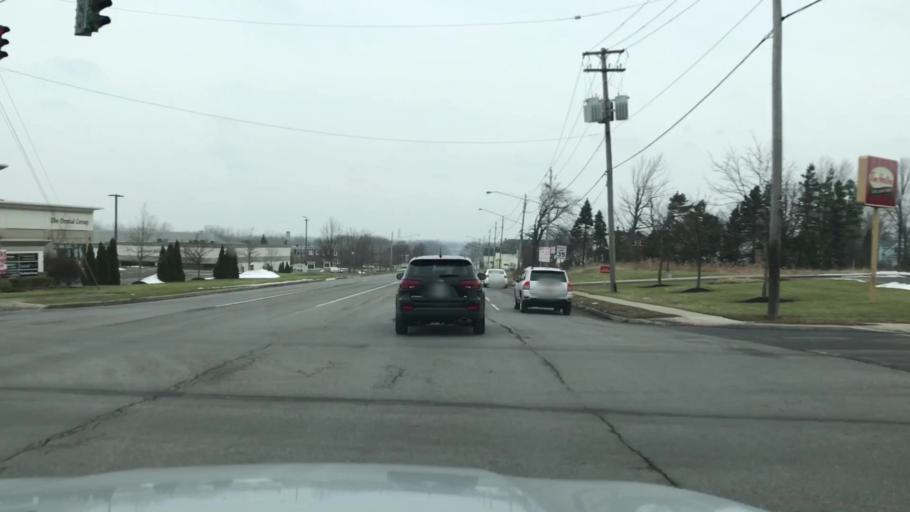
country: US
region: New York
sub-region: Erie County
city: Blasdell
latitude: 42.7967
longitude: -78.7949
